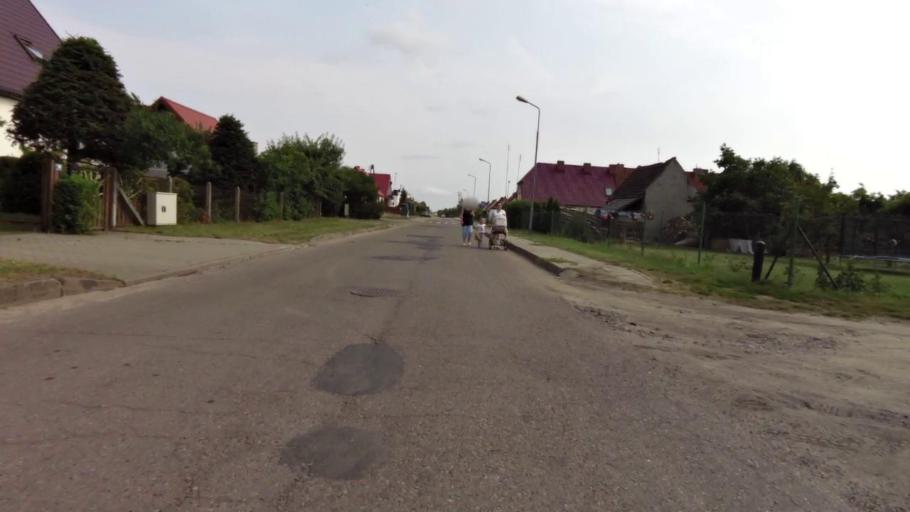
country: PL
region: West Pomeranian Voivodeship
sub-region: Powiat drawski
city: Zlocieniec
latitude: 53.5480
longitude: 15.9982
